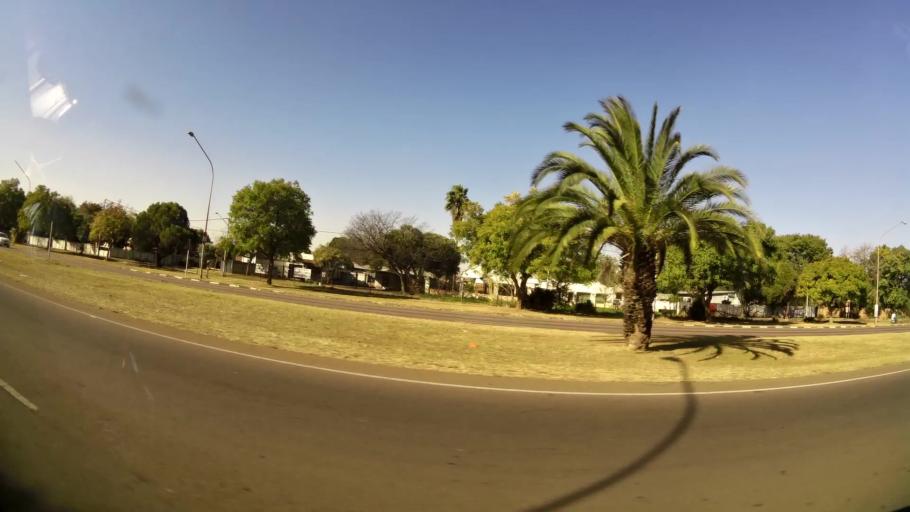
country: ZA
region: Gauteng
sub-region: City of Tshwane Metropolitan Municipality
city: Pretoria
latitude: -25.7272
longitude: 28.2583
